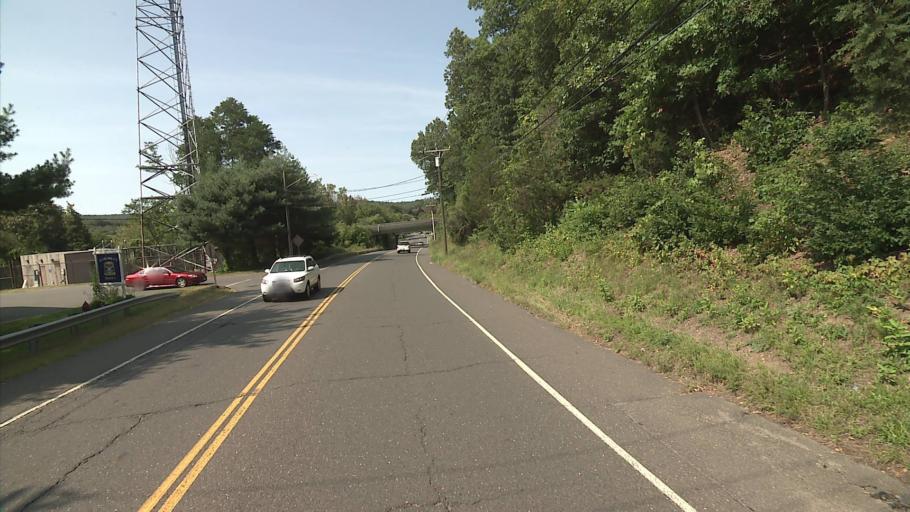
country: US
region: Connecticut
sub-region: New Haven County
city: Heritage Village
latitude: 41.4569
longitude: -73.2336
